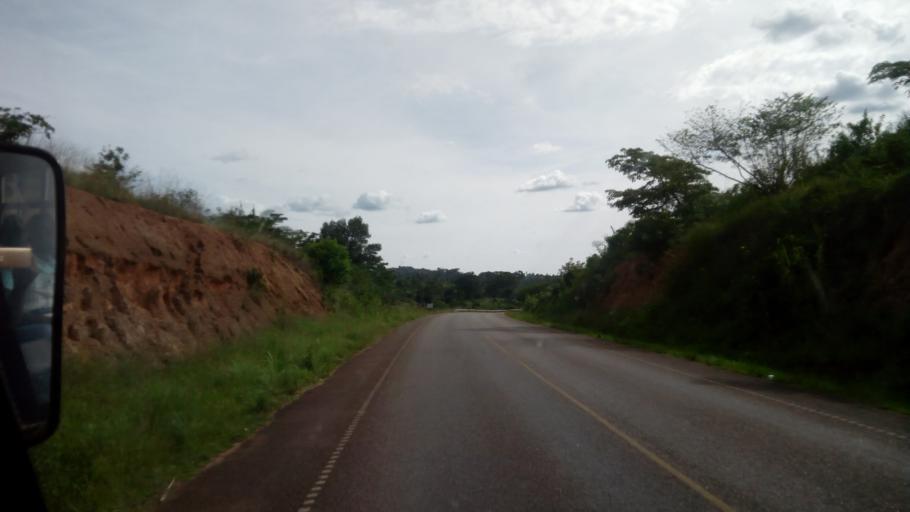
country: UG
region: Central Region
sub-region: Mubende District
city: Mubende
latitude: 0.4898
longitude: 31.2400
